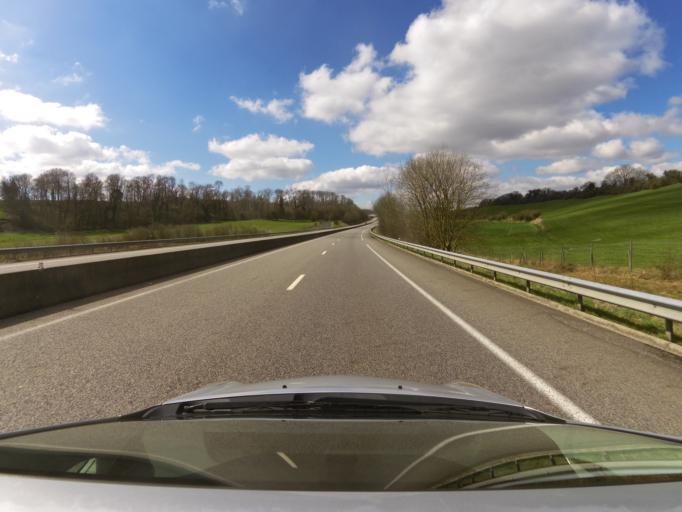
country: FR
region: Haute-Normandie
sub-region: Departement de la Seine-Maritime
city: Foucarmont
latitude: 49.8417
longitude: 1.5435
